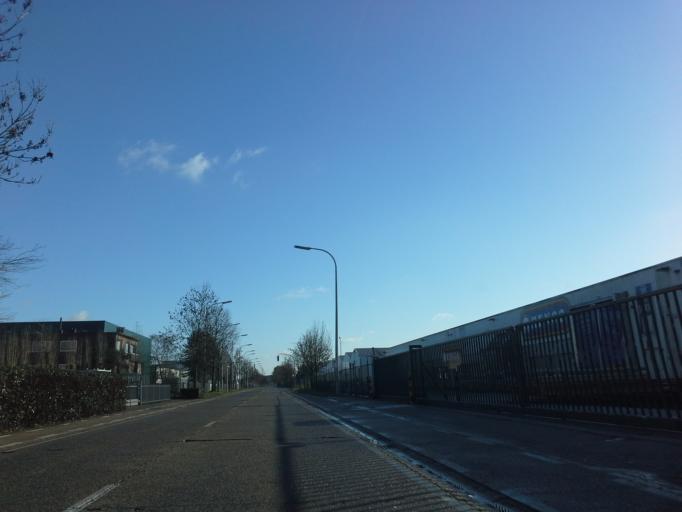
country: BE
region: Flanders
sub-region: Provincie Antwerpen
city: Herentals
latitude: 51.1645
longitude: 4.7980
